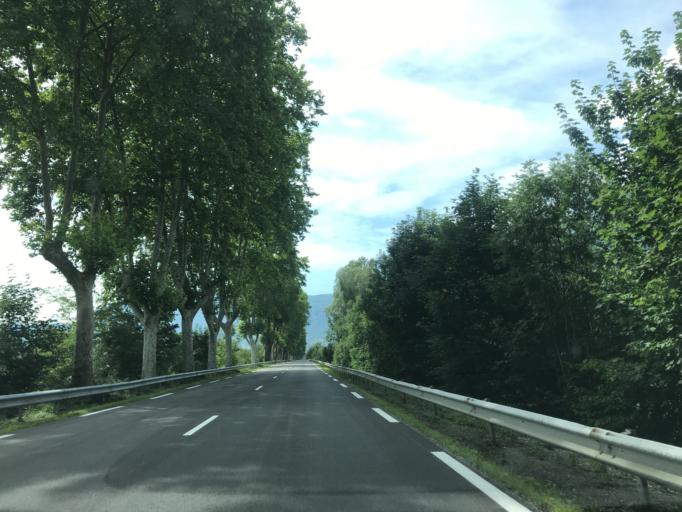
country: FR
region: Rhone-Alpes
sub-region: Departement de la Savoie
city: Aiton
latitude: 45.5568
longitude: 6.2347
